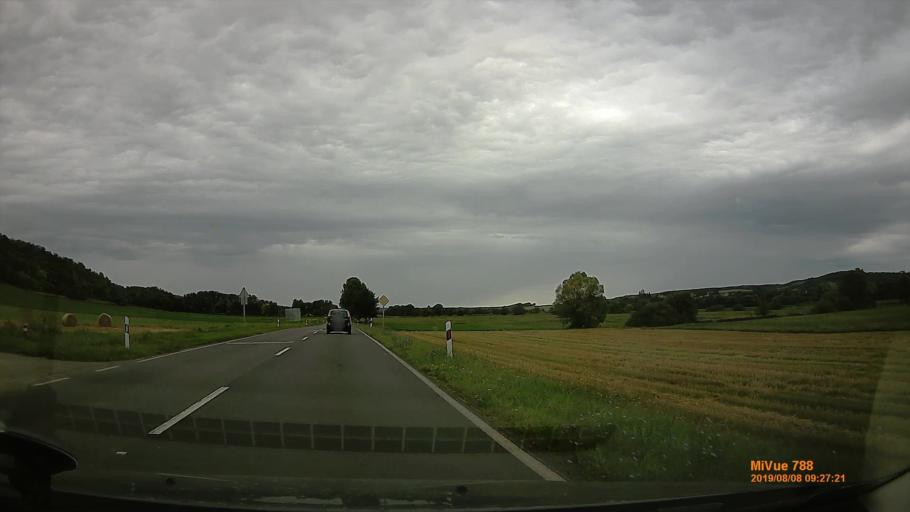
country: HU
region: Zala
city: Zalaegerszeg
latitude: 46.9470
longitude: 16.8492
